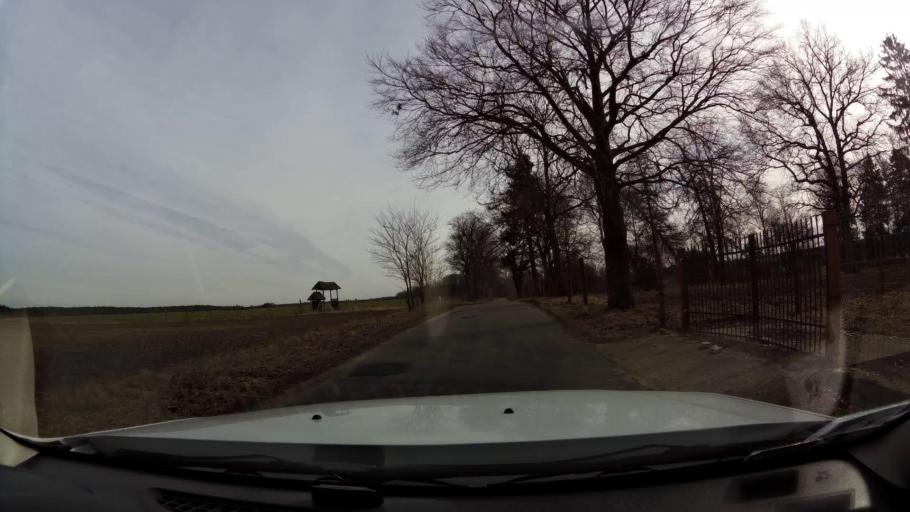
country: PL
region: West Pomeranian Voivodeship
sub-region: Powiat stargardzki
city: Insko
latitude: 53.4549
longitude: 15.6184
